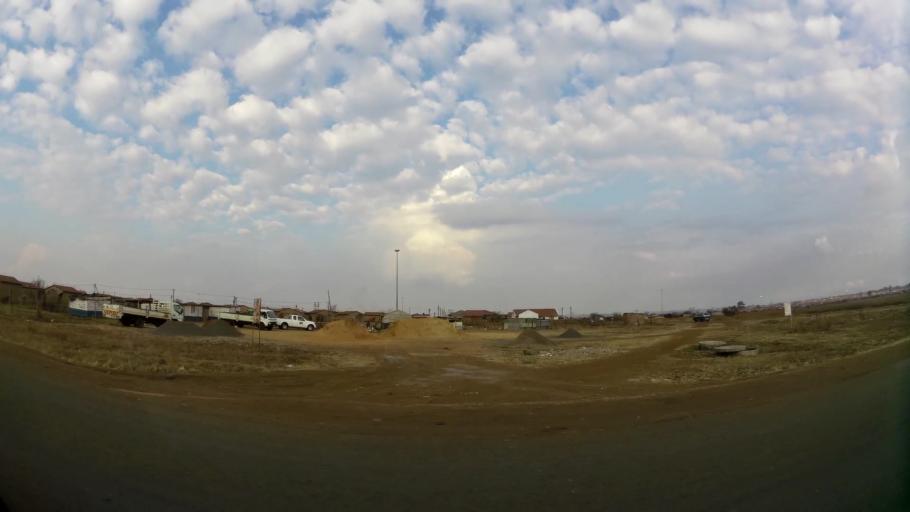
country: ZA
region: Gauteng
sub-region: Sedibeng District Municipality
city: Vereeniging
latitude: -26.6554
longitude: 27.8713
